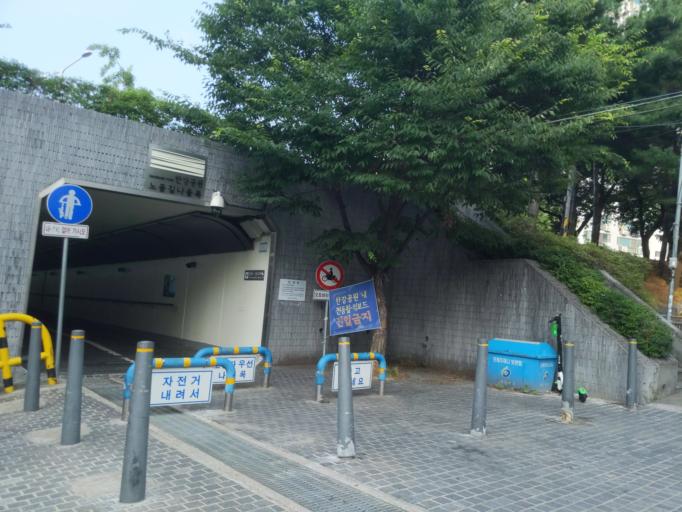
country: KR
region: Gyeonggi-do
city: Kwangmyong
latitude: 37.5352
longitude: 126.9039
